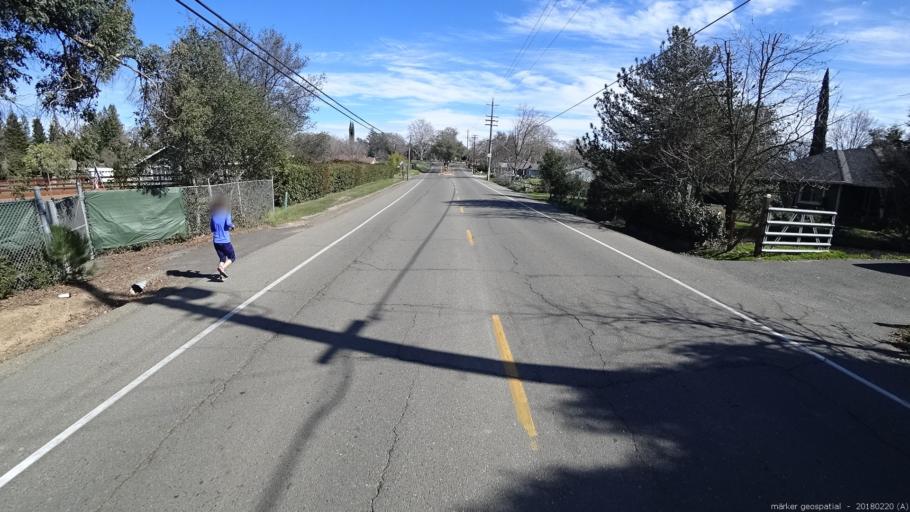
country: US
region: California
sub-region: Sacramento County
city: Orangevale
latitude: 38.6929
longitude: -121.2179
